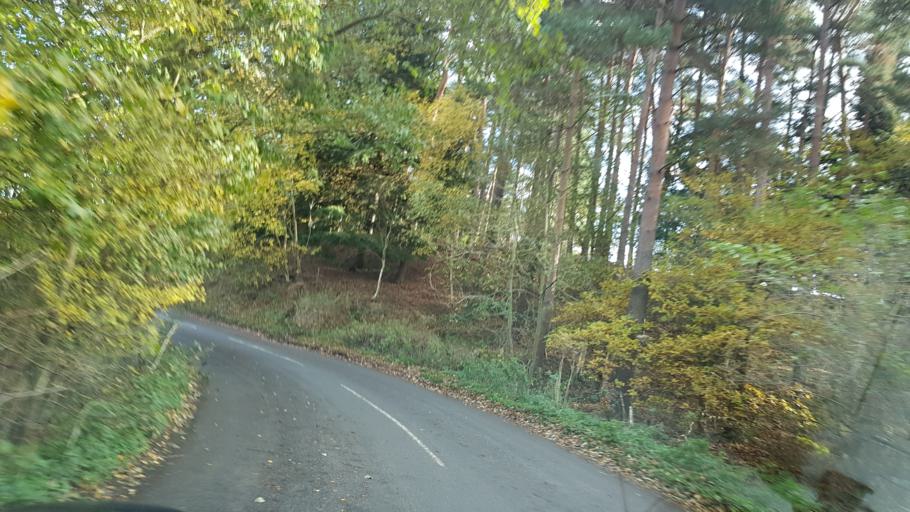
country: GB
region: England
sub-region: Surrey
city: Seale
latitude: 51.2222
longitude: -0.7068
